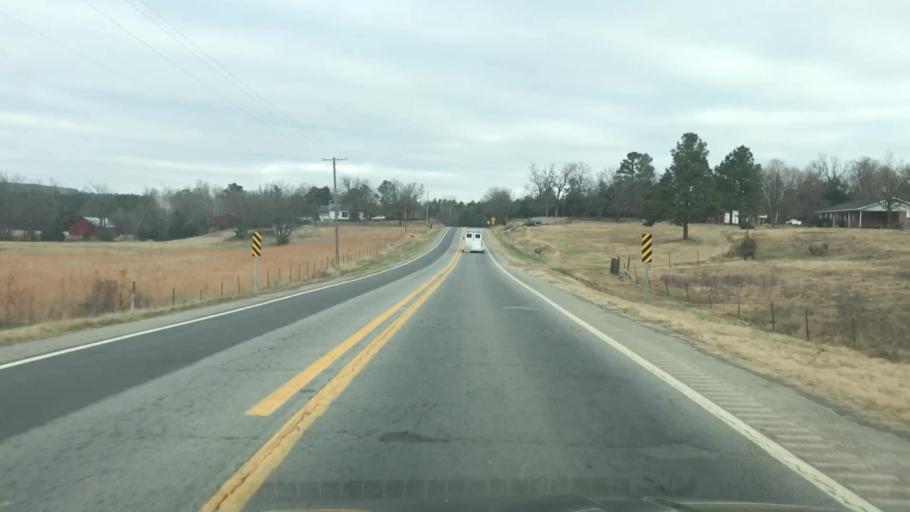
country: US
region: Arkansas
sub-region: Scott County
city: Waldron
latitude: 34.9478
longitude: -94.1046
